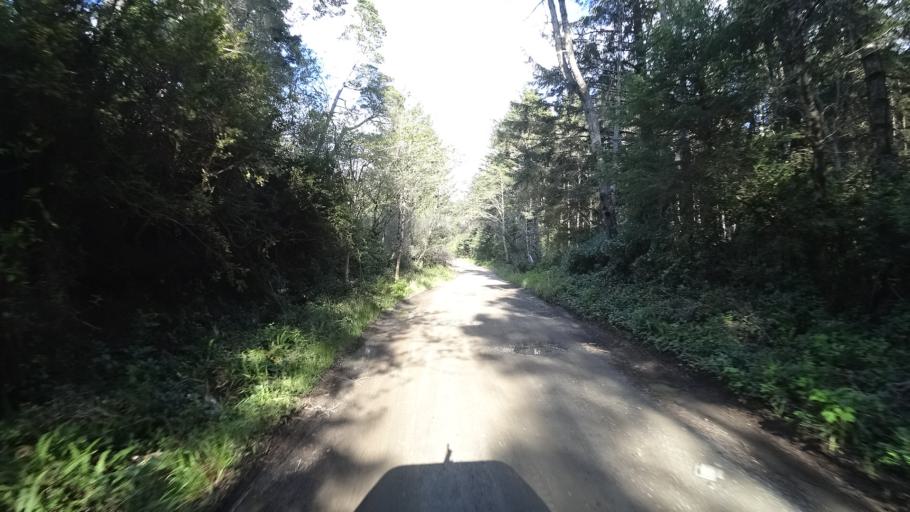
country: US
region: Oregon
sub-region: Douglas County
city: Reedsport
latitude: 43.7473
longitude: -124.1649
